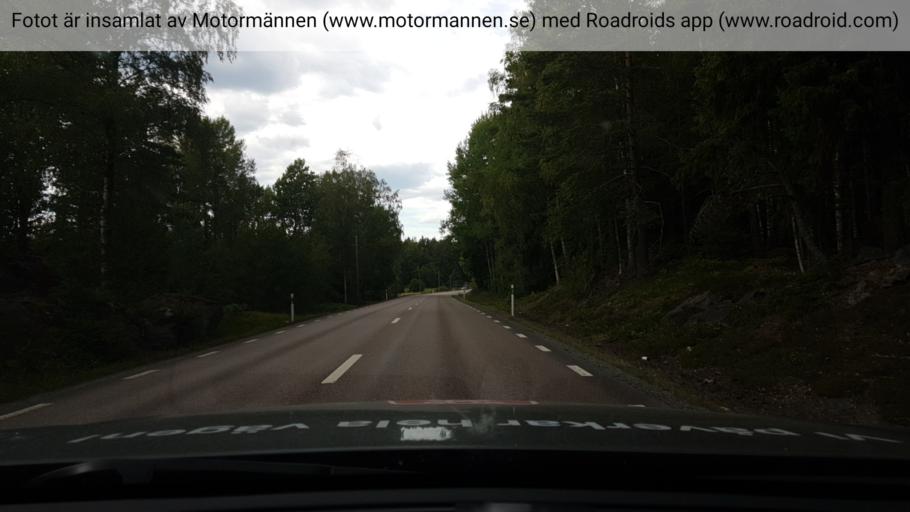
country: SE
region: Uppsala
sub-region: Enkopings Kommun
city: Irsta
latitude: 59.7862
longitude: 16.8361
